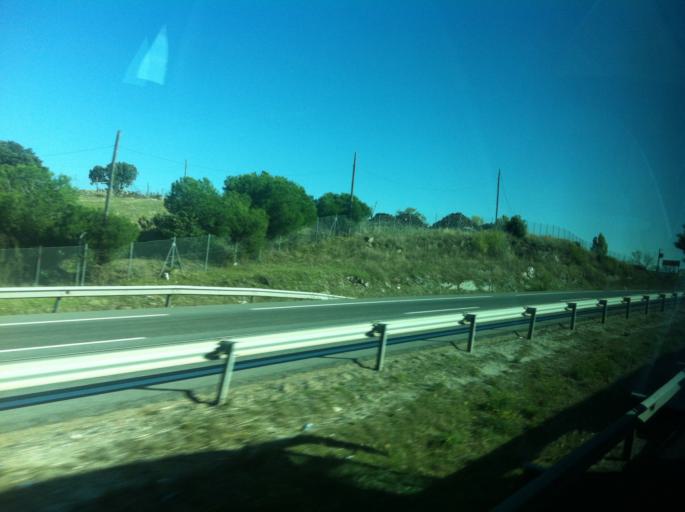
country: ES
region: Madrid
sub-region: Provincia de Madrid
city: Venturada
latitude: 40.7744
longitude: -3.6090
